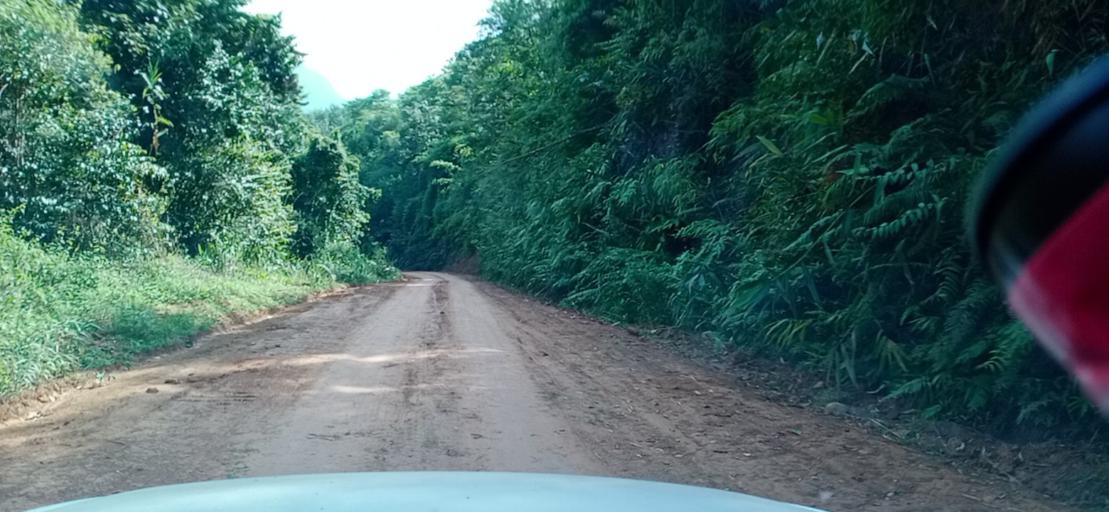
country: TH
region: Changwat Bueng Kan
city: Pak Khat
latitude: 18.6368
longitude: 103.2512
